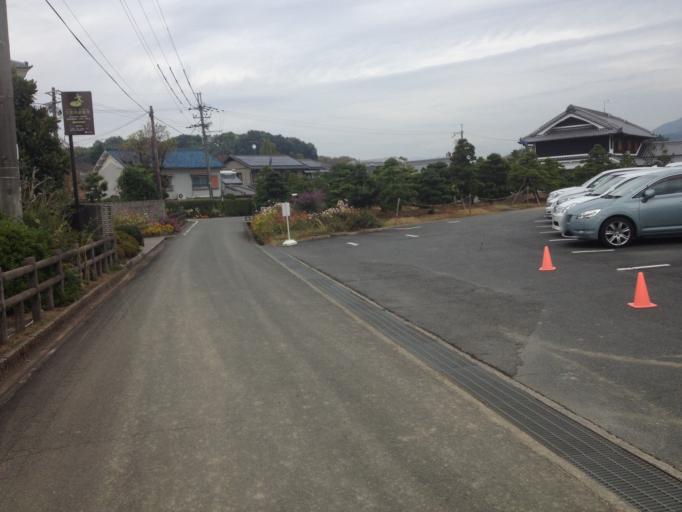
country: JP
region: Nara
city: Kashihara-shi
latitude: 34.4700
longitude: 135.8071
